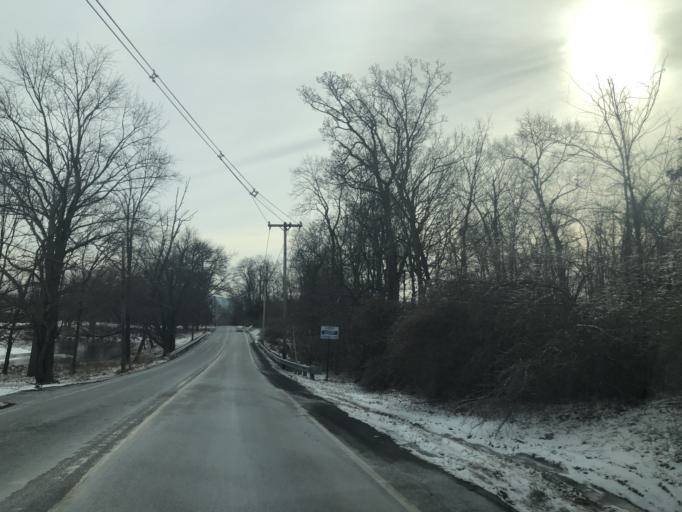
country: US
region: New Jersey
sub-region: Warren County
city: Belvidere
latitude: 40.9334
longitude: -75.0116
